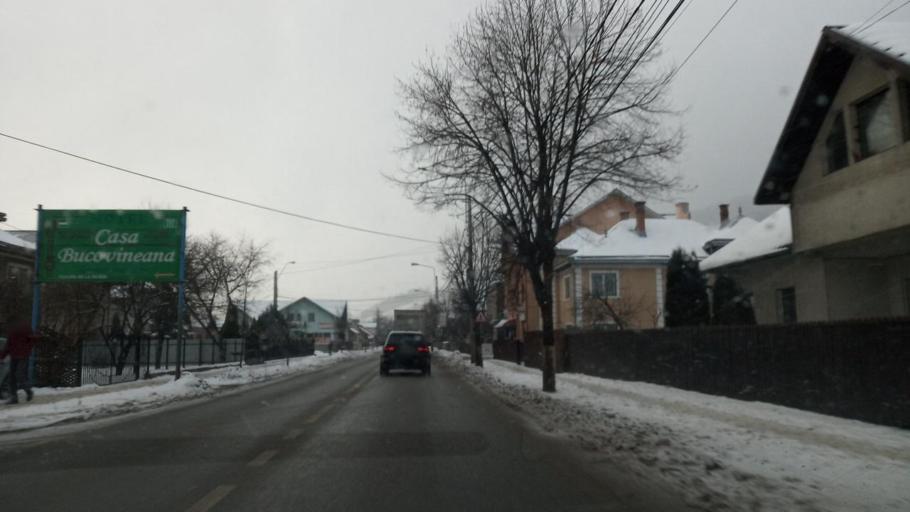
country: RO
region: Suceava
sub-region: Municipiul Vatra Dornei
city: Vatra Dornei
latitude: 47.3463
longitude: 25.3458
